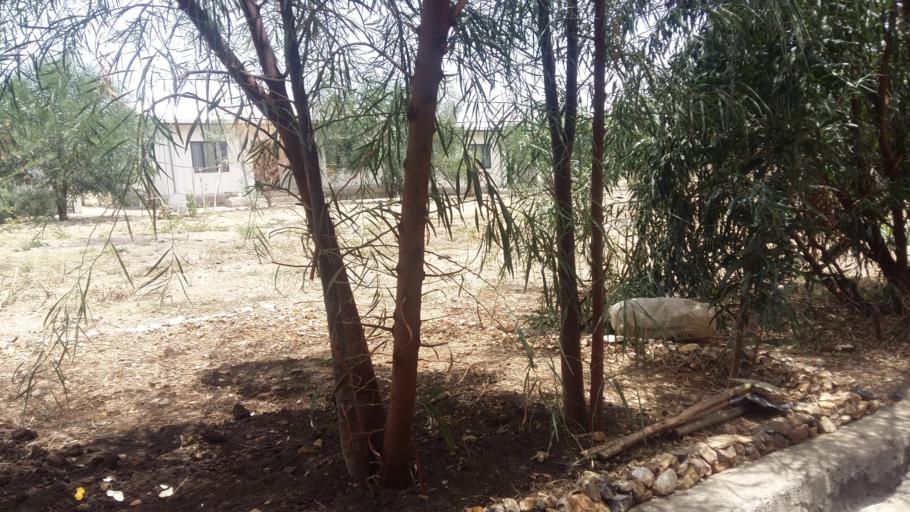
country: ET
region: Amhara
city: Were Ilu
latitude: 10.4221
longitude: 39.1147
